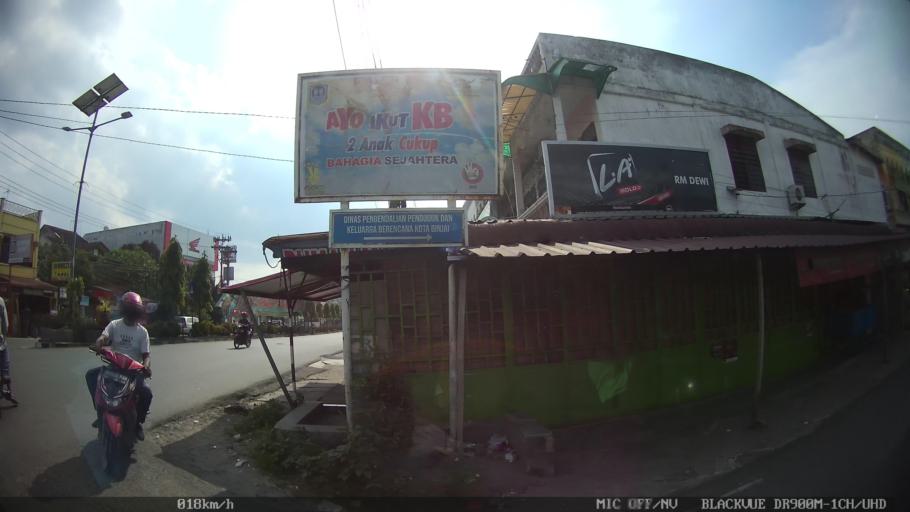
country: ID
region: North Sumatra
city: Binjai
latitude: 3.6090
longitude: 98.5017
